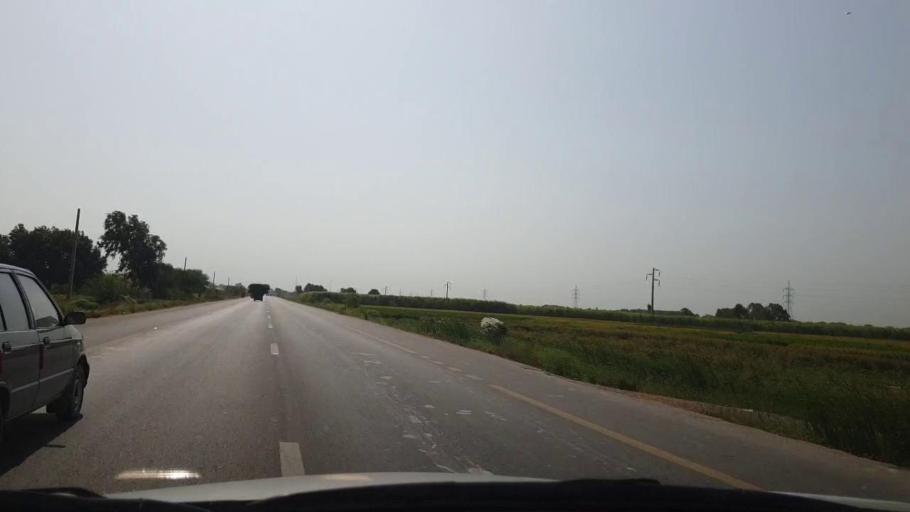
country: PK
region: Sindh
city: Tando Muhammad Khan
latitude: 25.1114
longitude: 68.5797
